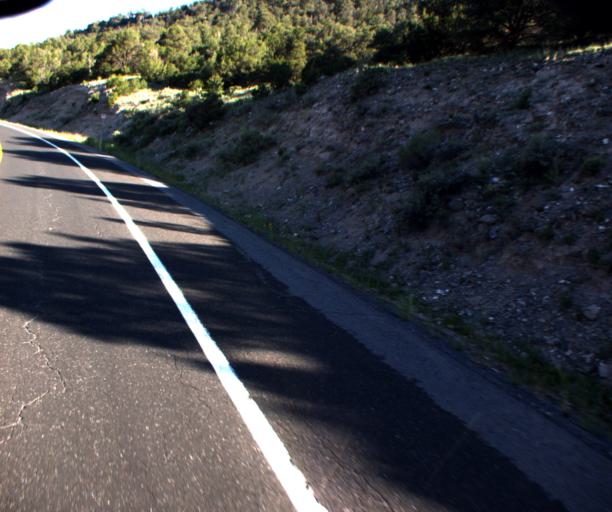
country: US
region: Arizona
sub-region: Apache County
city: Eagar
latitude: 34.0578
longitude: -109.1902
